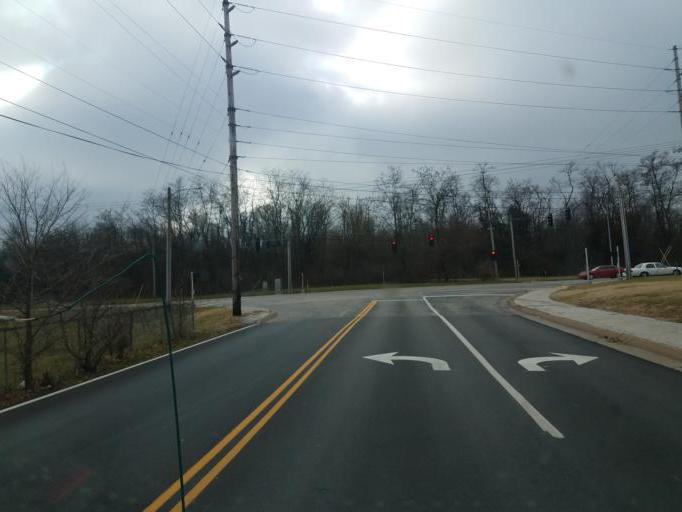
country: US
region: Missouri
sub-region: Greene County
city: Springfield
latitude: 37.2396
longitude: -93.2292
